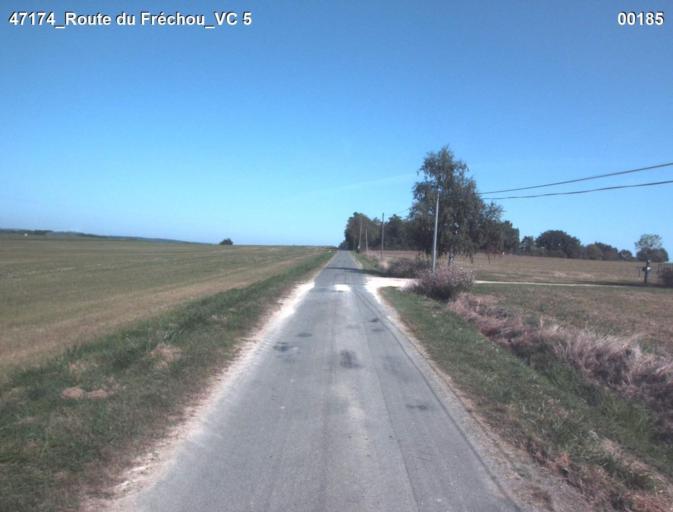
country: FR
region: Aquitaine
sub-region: Departement du Lot-et-Garonne
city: Nerac
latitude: 44.0630
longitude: 0.3359
